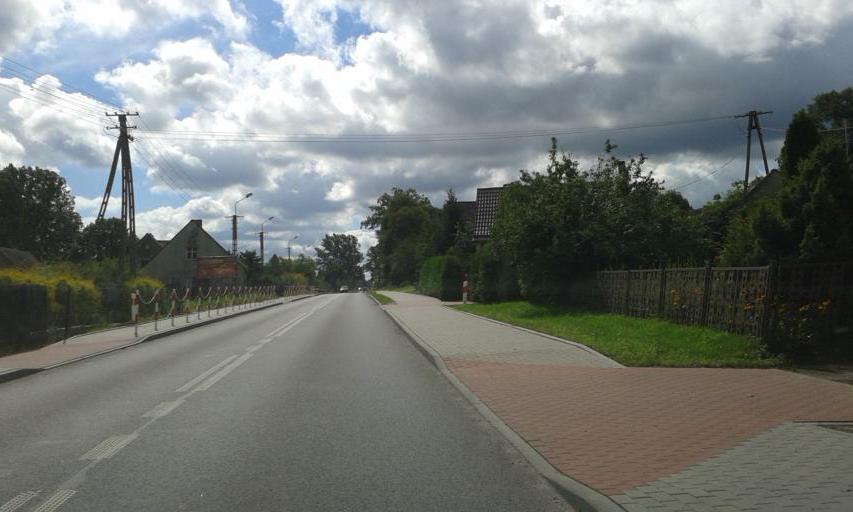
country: PL
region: West Pomeranian Voivodeship
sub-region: Powiat drawski
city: Czaplinek
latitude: 53.5211
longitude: 16.3105
